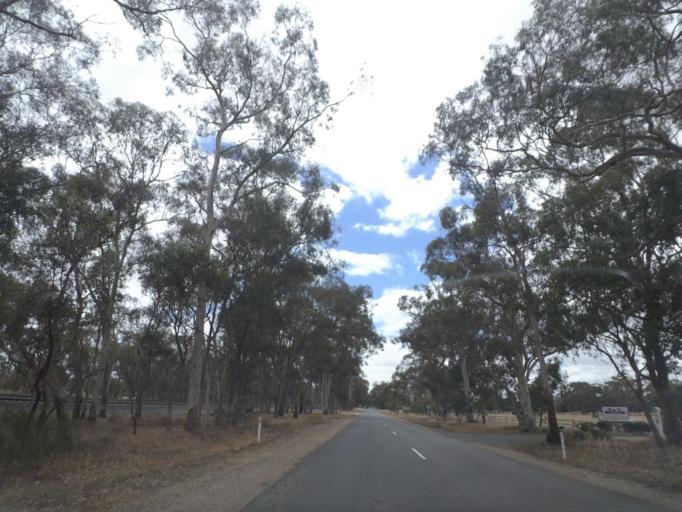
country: AU
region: Victoria
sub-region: Murrindindi
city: Kinglake West
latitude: -36.9434
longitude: 145.1743
